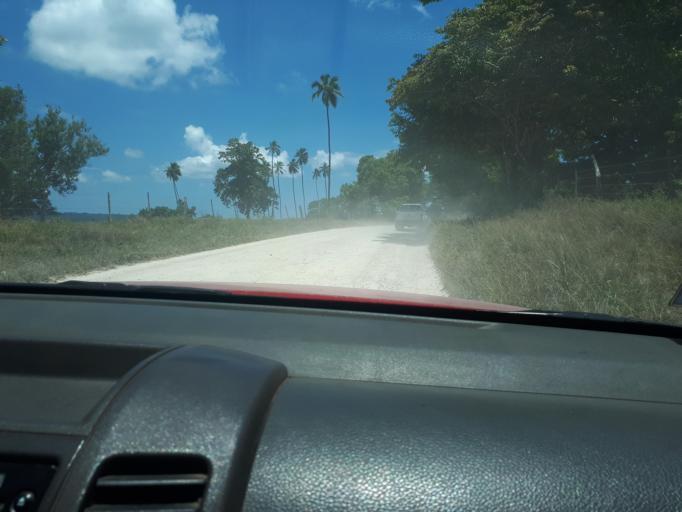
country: VU
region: Sanma
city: Luganville
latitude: -15.5779
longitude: 167.1226
